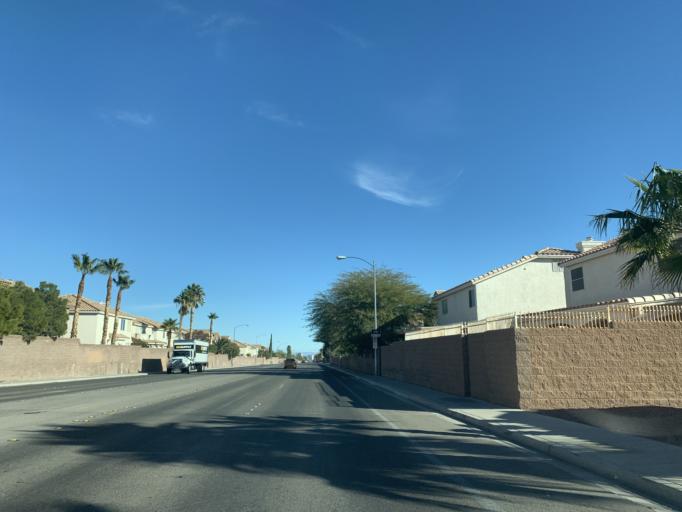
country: US
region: Nevada
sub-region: Clark County
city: Summerlin South
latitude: 36.1225
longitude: -115.3097
